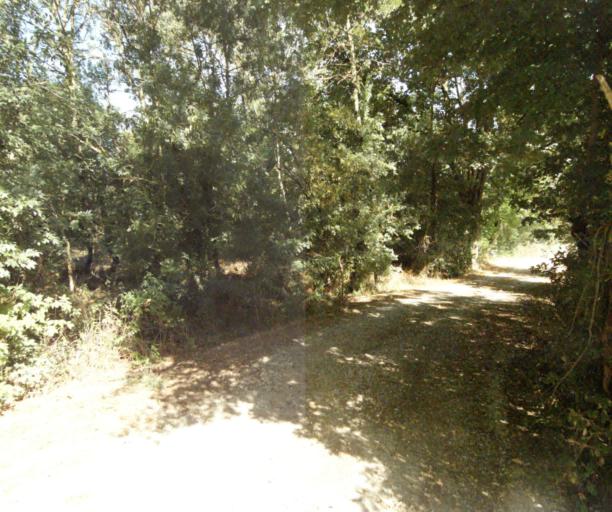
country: FR
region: Midi-Pyrenees
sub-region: Departement du Tarn
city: Soual
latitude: 43.5229
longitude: 2.0790
